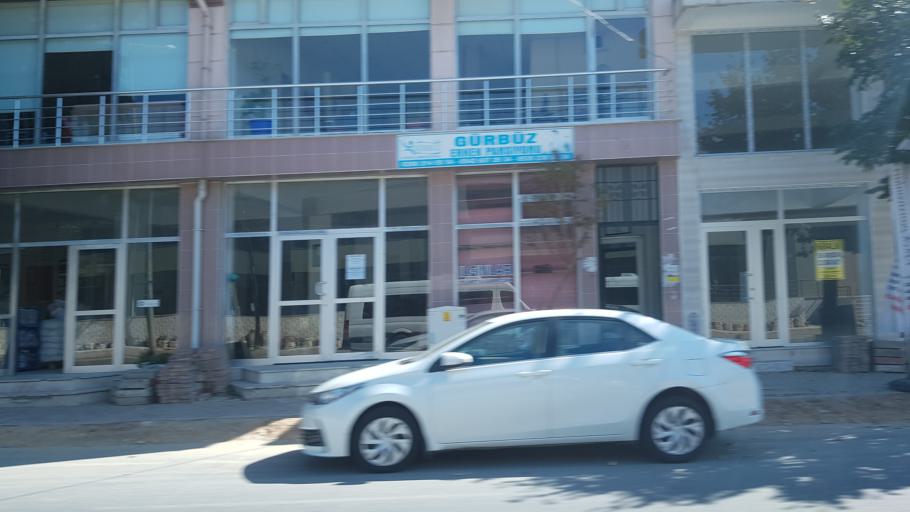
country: TR
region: Kirklareli
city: Kirklareli
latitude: 41.7418
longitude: 27.2169
